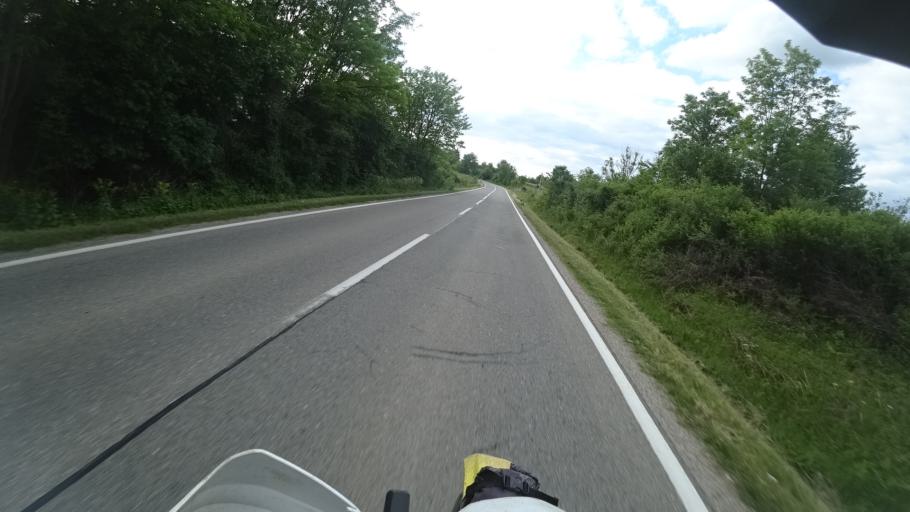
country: HR
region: Licko-Senjska
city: Gospic
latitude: 44.5119
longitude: 15.4270
